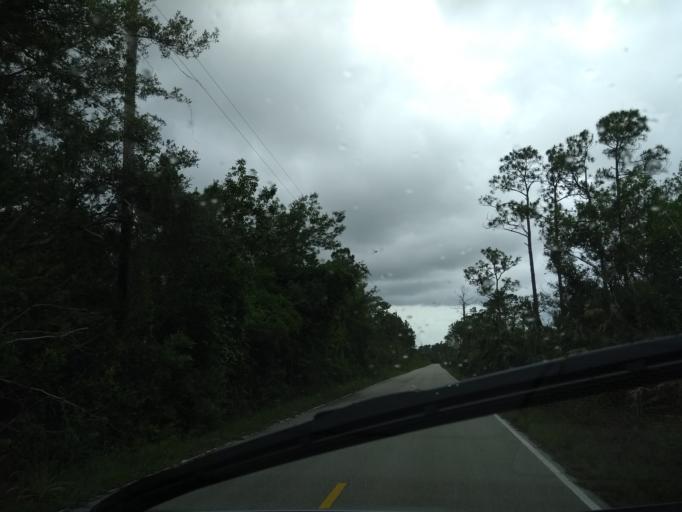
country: US
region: Florida
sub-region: Miami-Dade County
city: The Hammocks
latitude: 25.7496
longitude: -80.9366
